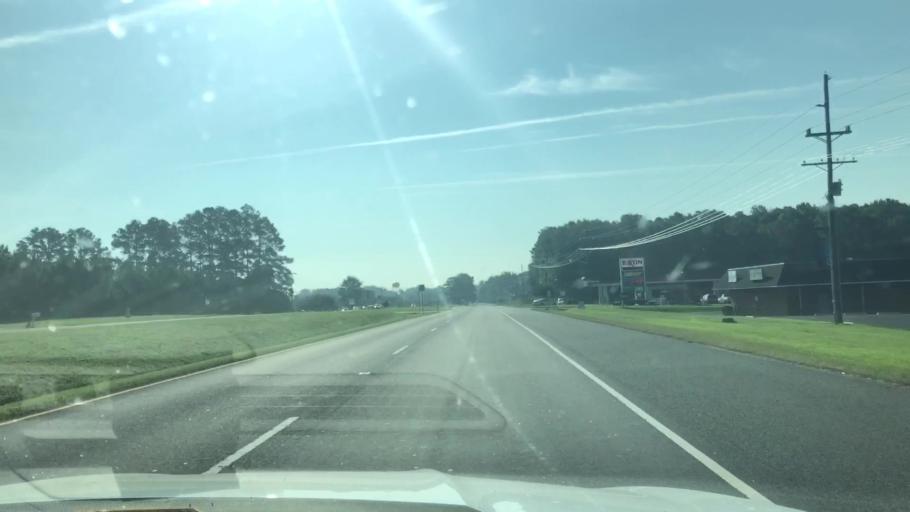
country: US
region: Virginia
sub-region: Richmond County
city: Warsaw
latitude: 37.9646
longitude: -76.7854
